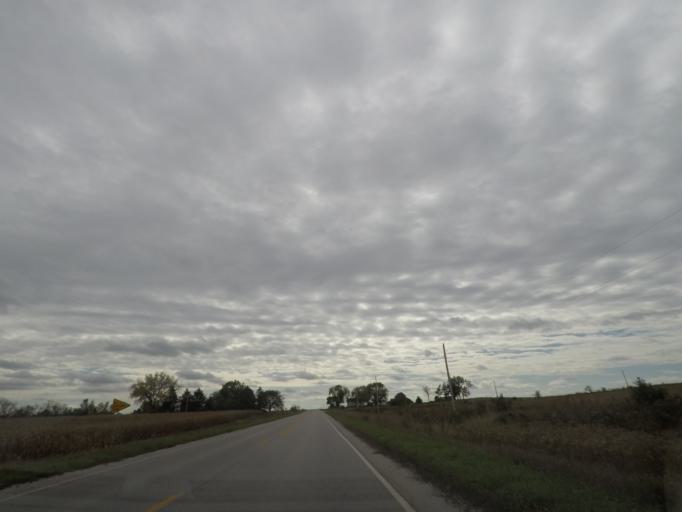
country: US
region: Iowa
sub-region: Story County
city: Huxley
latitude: 41.8647
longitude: -93.5317
